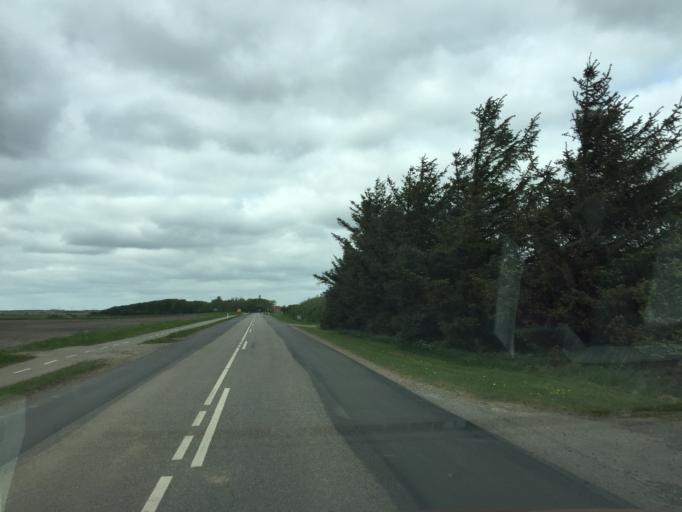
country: DK
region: Central Jutland
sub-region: Ringkobing-Skjern Kommune
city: Ringkobing
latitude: 56.0415
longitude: 8.3157
